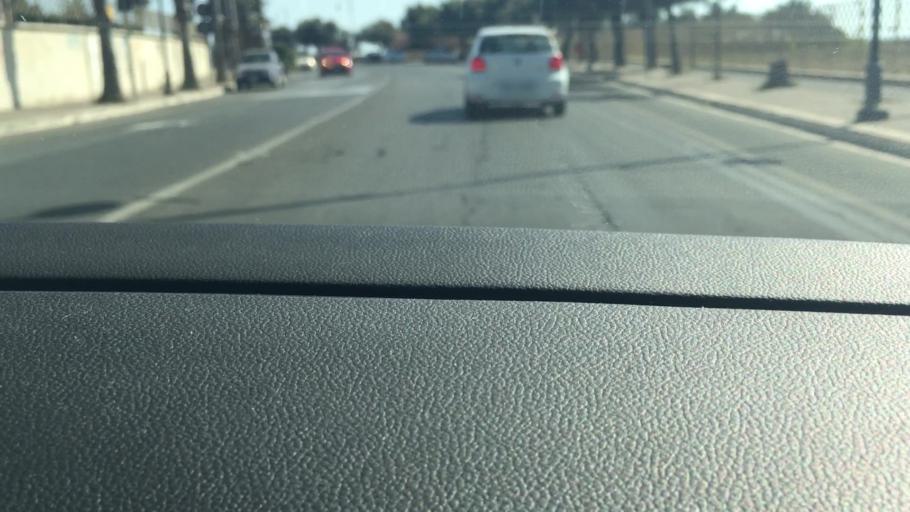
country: IT
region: Latium
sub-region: Citta metropolitana di Roma Capitale
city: Anzio
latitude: 41.4502
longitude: 12.6201
